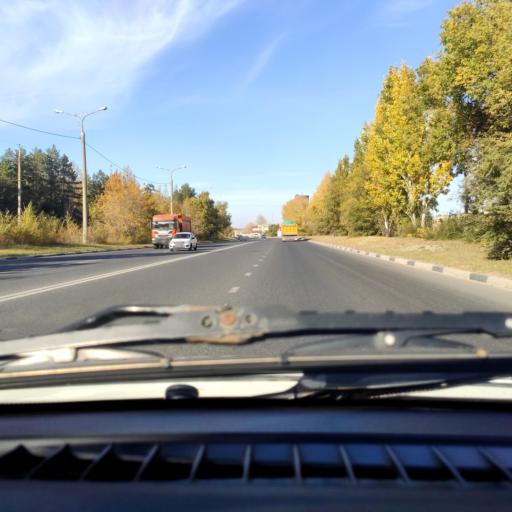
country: RU
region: Samara
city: Zhigulevsk
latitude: 53.4905
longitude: 49.4743
